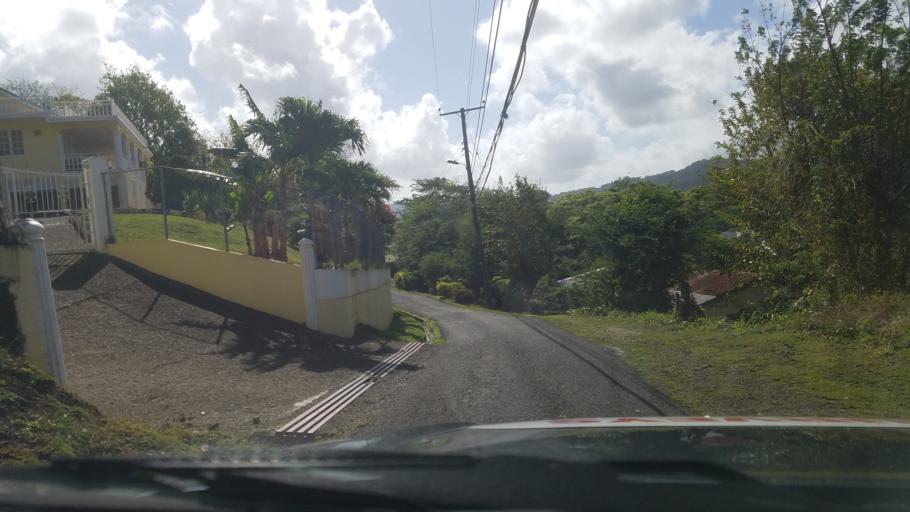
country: LC
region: Castries Quarter
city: Castries
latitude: 14.0193
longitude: -60.9999
